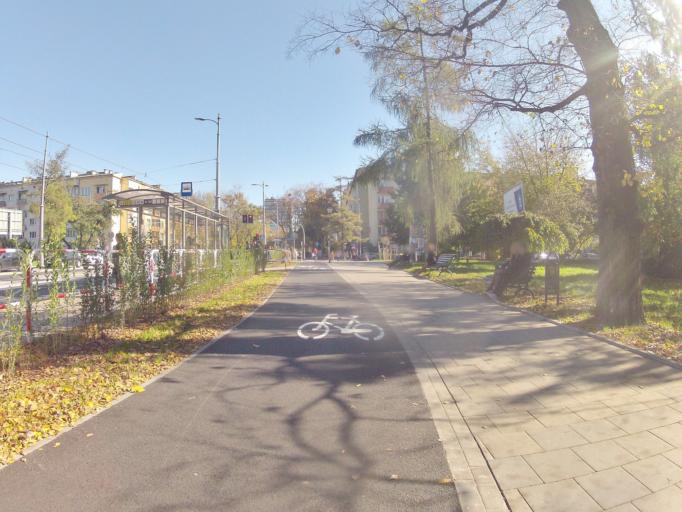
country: PL
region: Lesser Poland Voivodeship
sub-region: Krakow
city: Krakow
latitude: 50.0743
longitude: 19.9093
